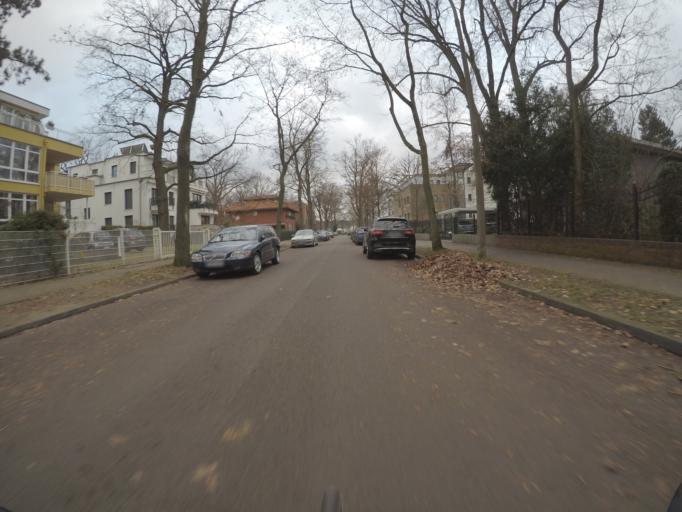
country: DE
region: Berlin
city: Grunau
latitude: 52.4152
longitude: 13.5901
